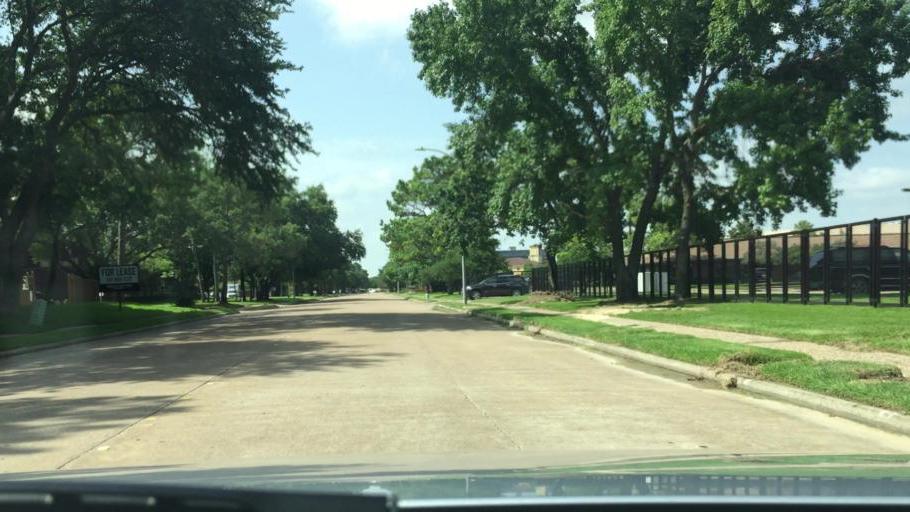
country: US
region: Texas
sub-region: Harris County
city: Hudson
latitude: 29.8492
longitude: -95.4949
